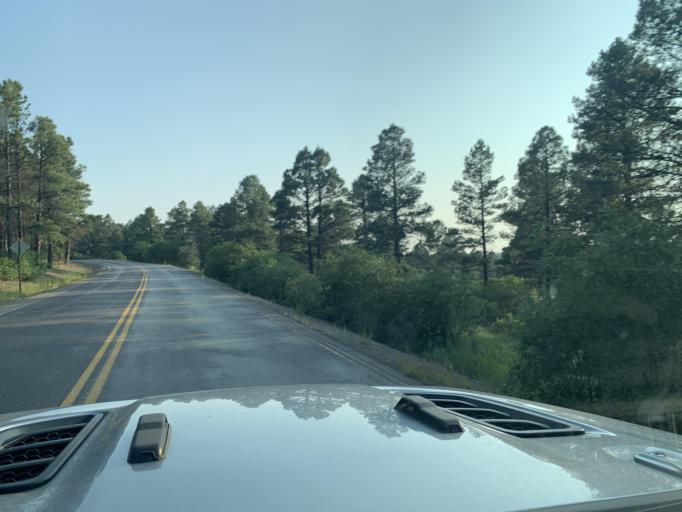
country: US
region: Colorado
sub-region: Archuleta County
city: Pagosa Springs
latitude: 37.2799
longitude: -107.0965
